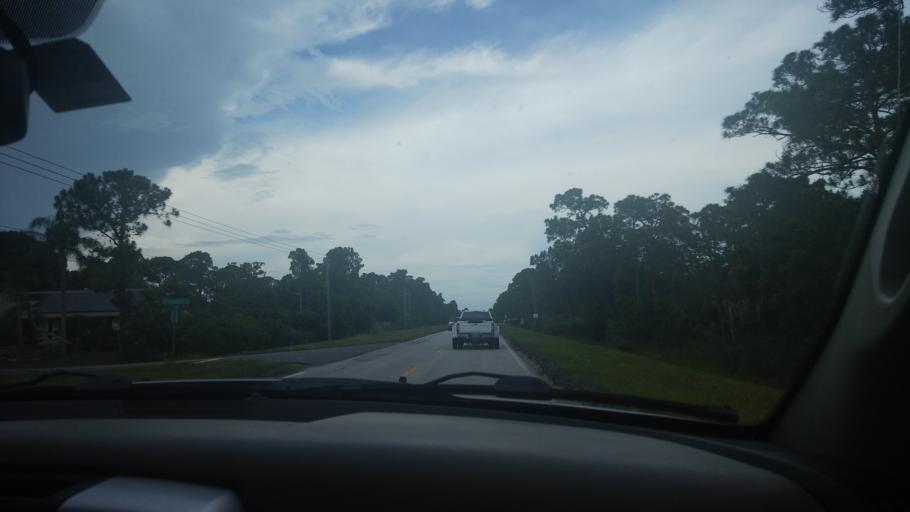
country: US
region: Florida
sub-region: Brevard County
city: Grant-Valkaria
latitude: 27.9396
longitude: -80.6228
